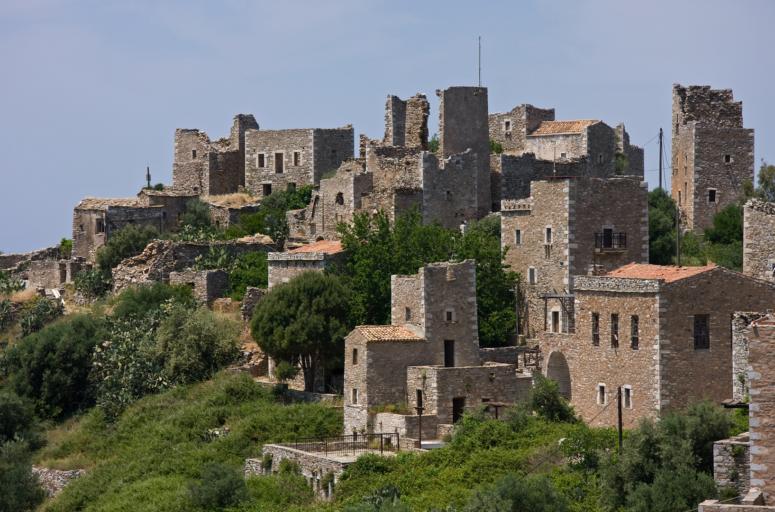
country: GR
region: Peloponnese
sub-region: Nomos Lakonias
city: Gytheio
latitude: 36.4524
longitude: 22.4678
